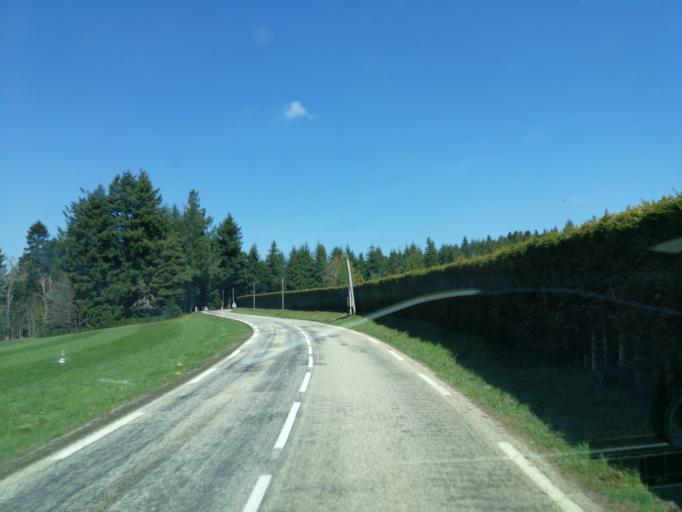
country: FR
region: Rhone-Alpes
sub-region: Departement de l'Ardeche
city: Saint-Agreve
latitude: 45.0191
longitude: 4.4072
